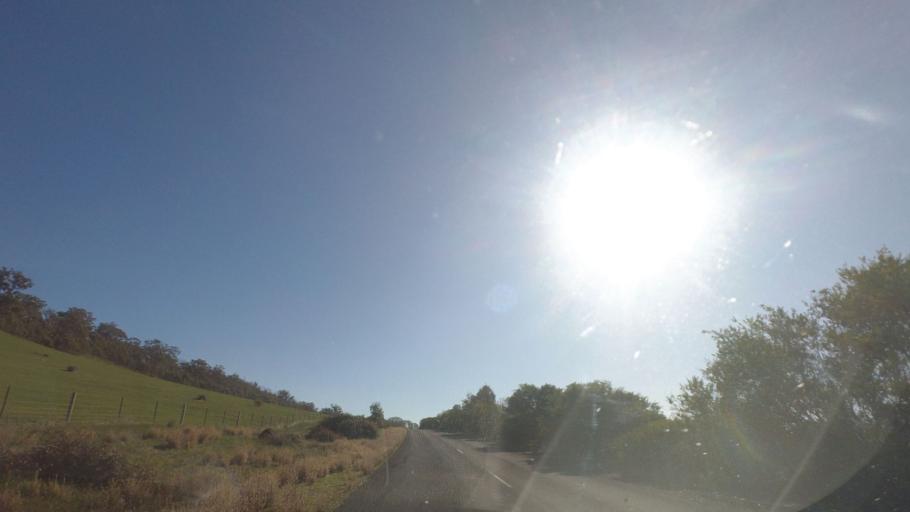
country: AU
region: Victoria
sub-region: Mount Alexander
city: Castlemaine
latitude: -37.0385
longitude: 144.2784
